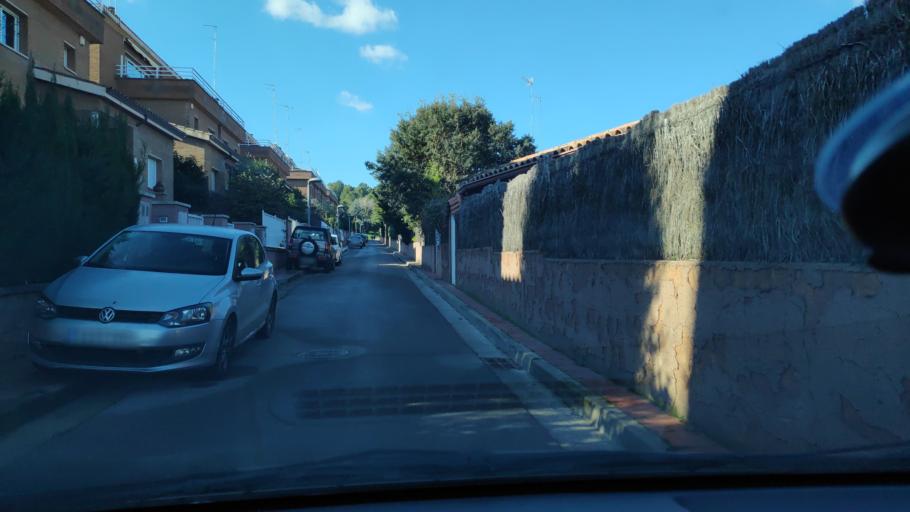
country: ES
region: Catalonia
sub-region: Provincia de Barcelona
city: Sant Quirze del Valles
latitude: 41.5245
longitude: 2.0732
